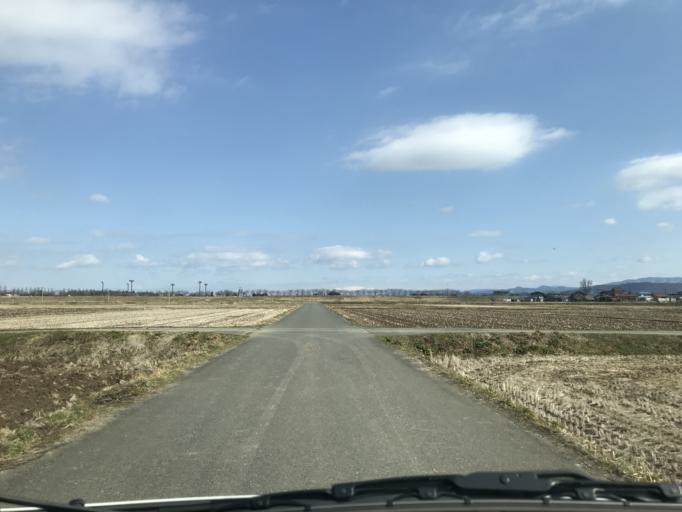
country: JP
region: Iwate
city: Mizusawa
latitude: 39.0488
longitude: 141.1402
